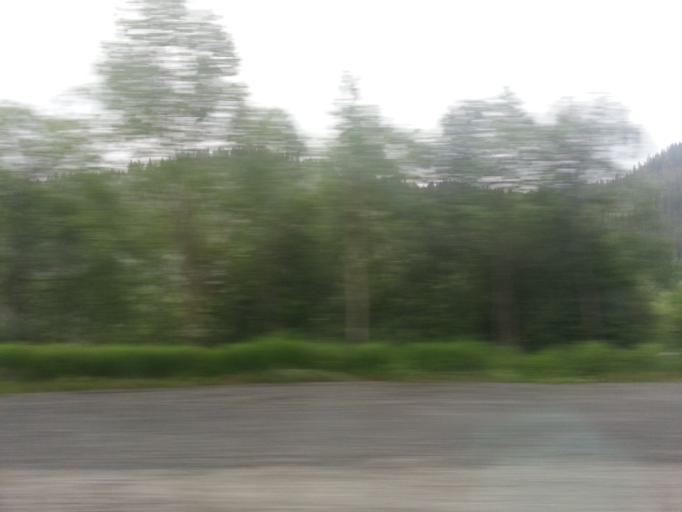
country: NO
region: Sor-Trondelag
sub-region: Midtre Gauldal
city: Storen
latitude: 62.9867
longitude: 10.2380
